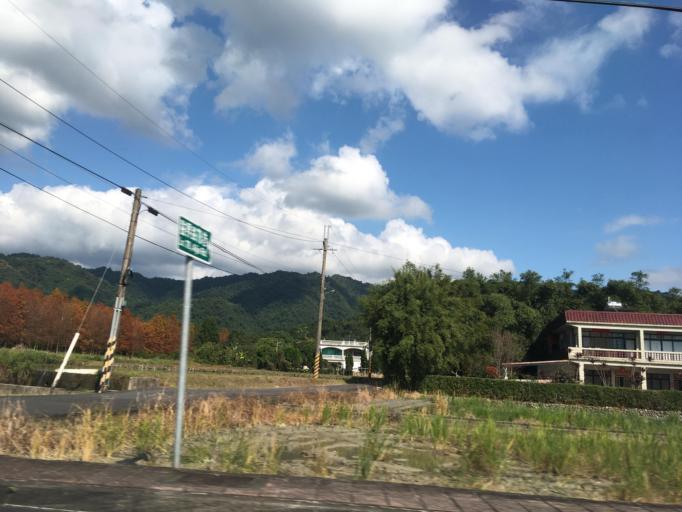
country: TW
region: Taiwan
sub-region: Yilan
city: Yilan
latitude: 24.7486
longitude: 121.6874
